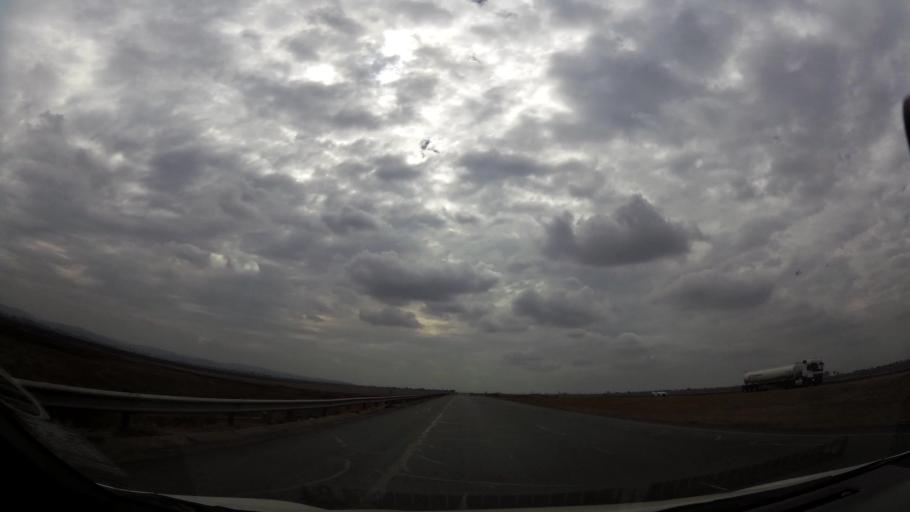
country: ZA
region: Gauteng
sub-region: Ekurhuleni Metropolitan Municipality
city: Germiston
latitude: -26.3812
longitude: 28.0877
